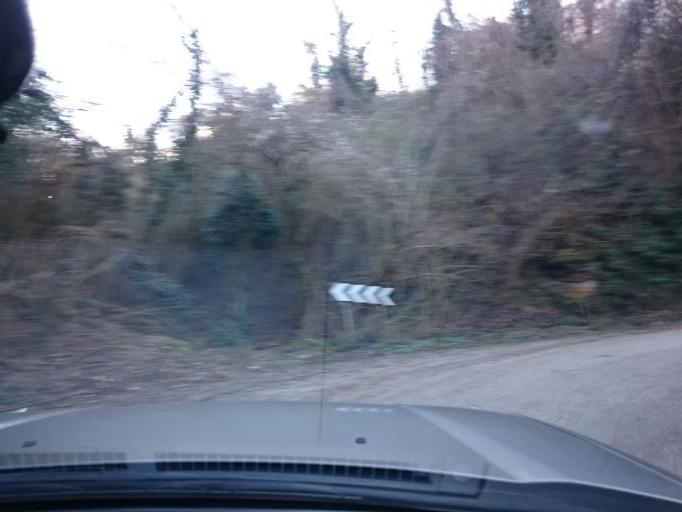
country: IT
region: Veneto
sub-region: Provincia di Padova
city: Torreglia
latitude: 45.3369
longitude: 11.7062
